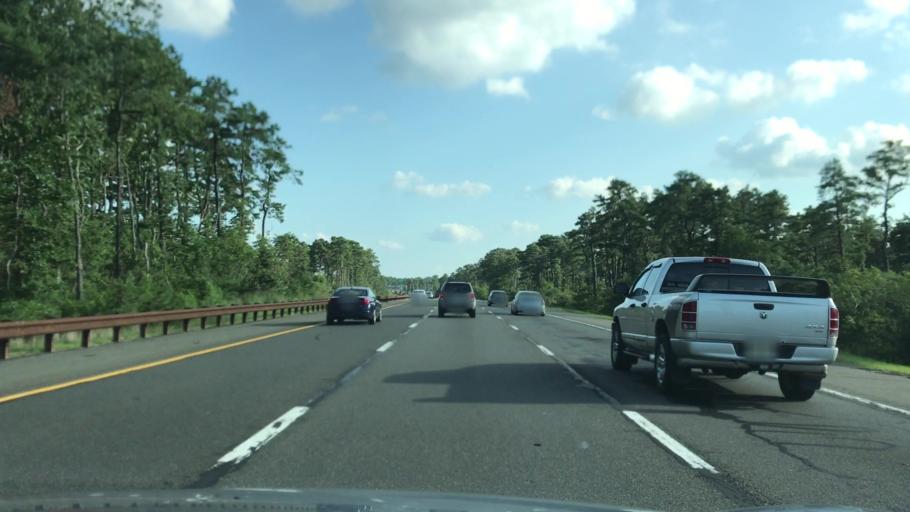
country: US
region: New Jersey
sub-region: Ocean County
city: South Toms River
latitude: 39.9159
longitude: -74.2116
